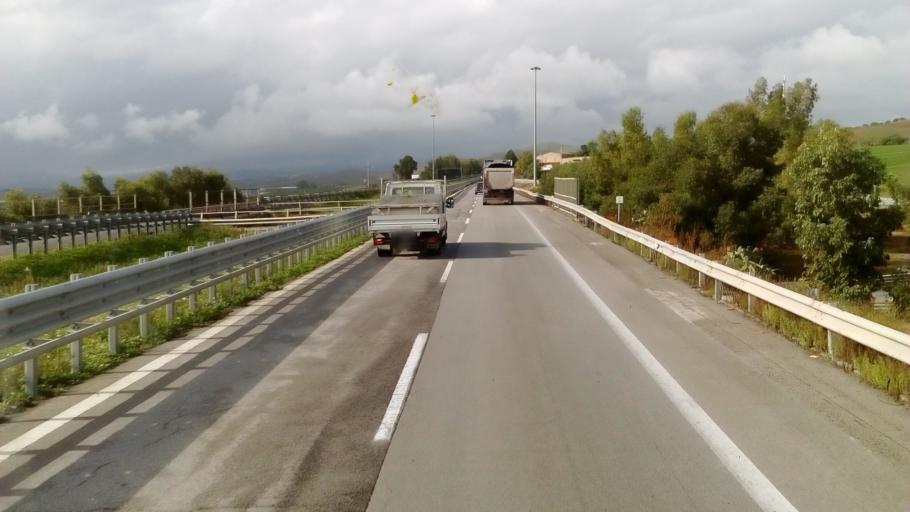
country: IT
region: Sicily
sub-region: Enna
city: Assoro
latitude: 37.5707
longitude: 14.4768
